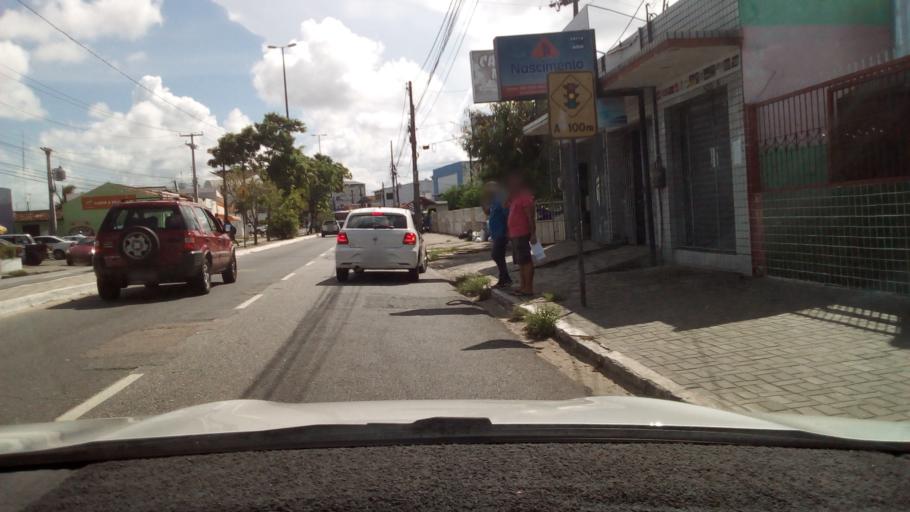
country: BR
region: Paraiba
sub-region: Joao Pessoa
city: Joao Pessoa
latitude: -7.1368
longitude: -34.8864
